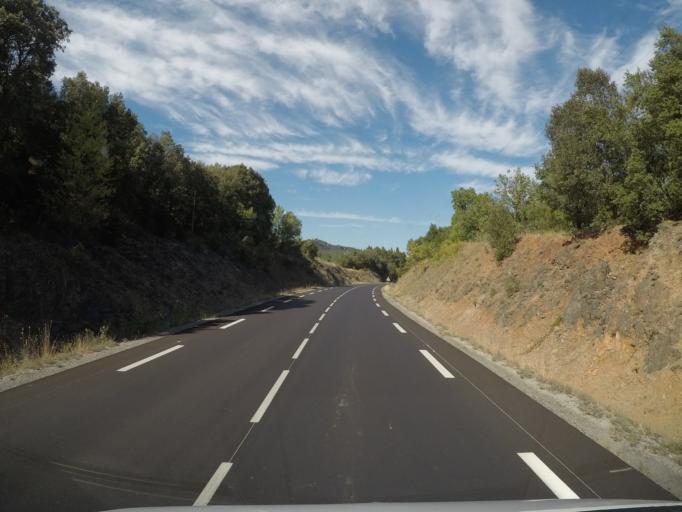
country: FR
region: Languedoc-Roussillon
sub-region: Departement du Gard
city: Sauve
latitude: 43.9740
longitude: 3.9248
